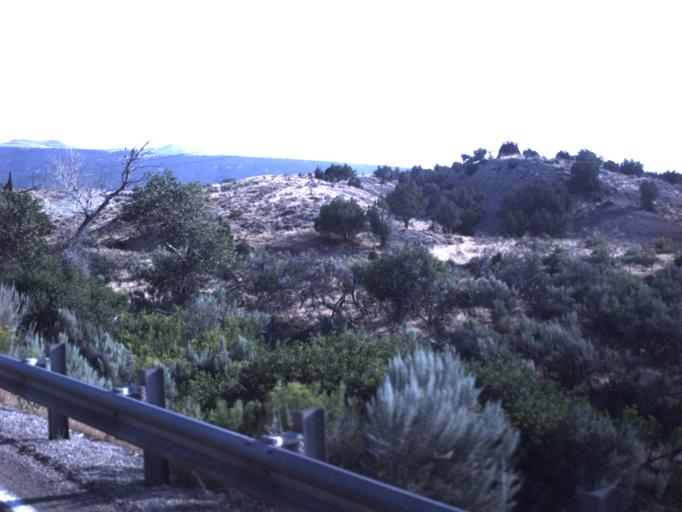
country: US
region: Utah
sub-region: Uintah County
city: Vernal
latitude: 40.6011
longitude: -109.4660
